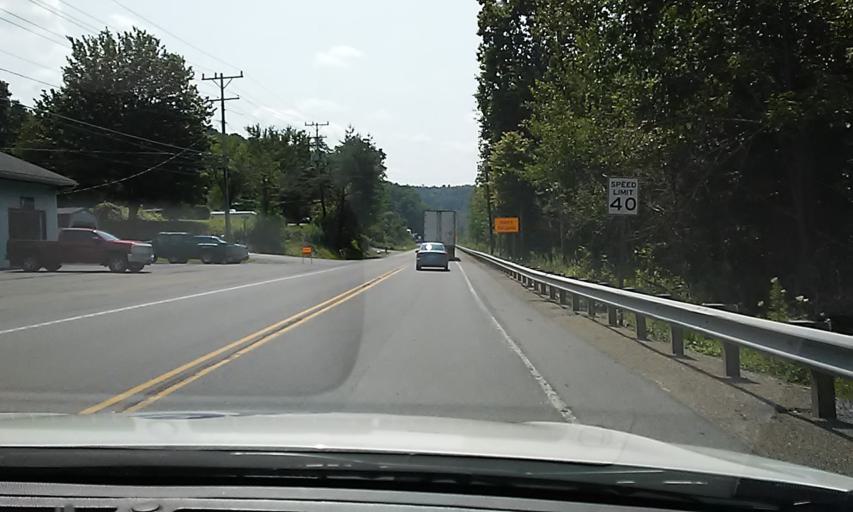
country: US
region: Pennsylvania
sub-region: Elk County
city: Ridgway
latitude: 41.4307
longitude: -78.7106
